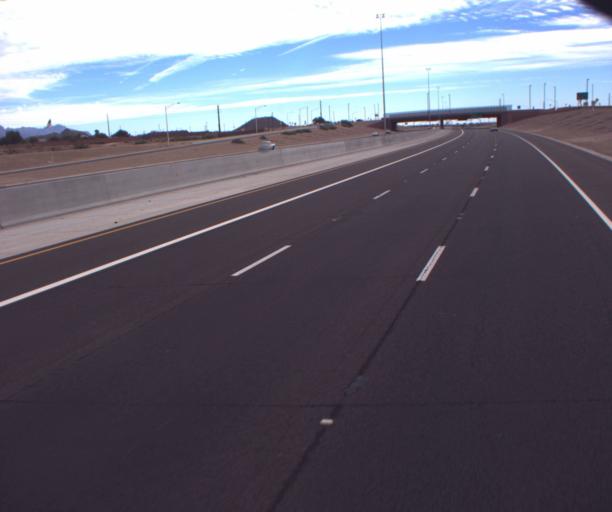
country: US
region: Arizona
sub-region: Pinal County
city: Apache Junction
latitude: 33.4538
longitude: -111.6726
